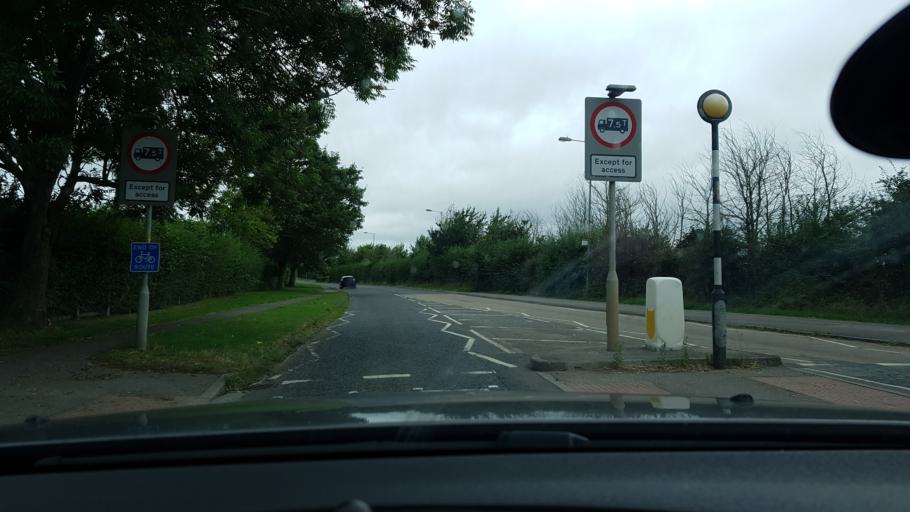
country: GB
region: England
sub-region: Wiltshire
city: Chippenham
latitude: 51.4498
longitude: -2.0938
